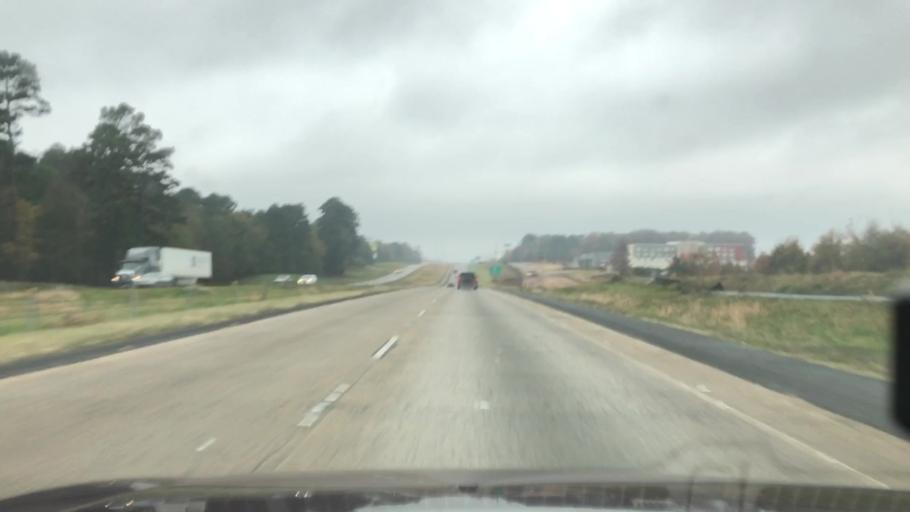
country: US
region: Louisiana
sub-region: Lincoln Parish
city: Ruston
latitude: 32.5405
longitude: -92.6015
